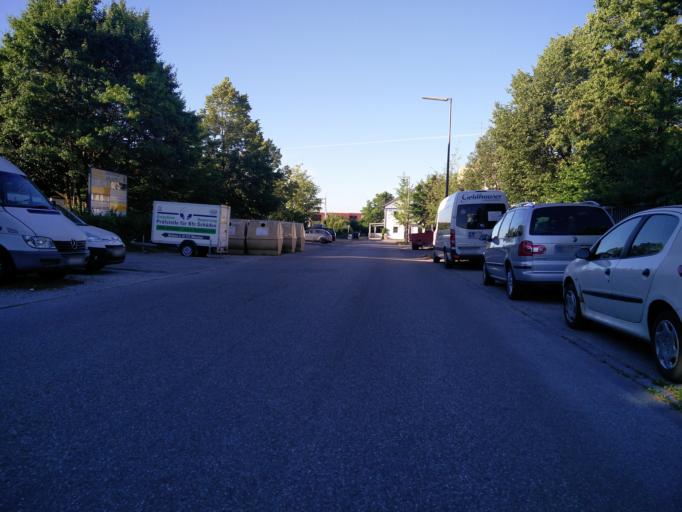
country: DE
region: Bavaria
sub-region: Upper Bavaria
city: Unterhaching
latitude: 48.0886
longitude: 11.6300
